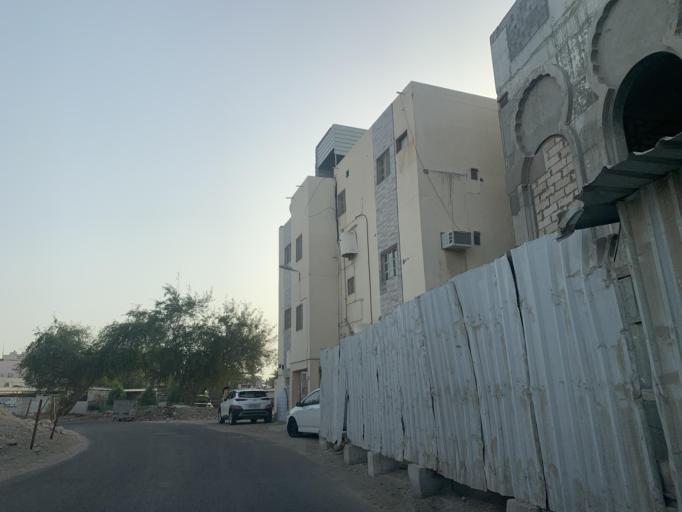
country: BH
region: Northern
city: Madinat `Isa
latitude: 26.1603
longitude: 50.5149
